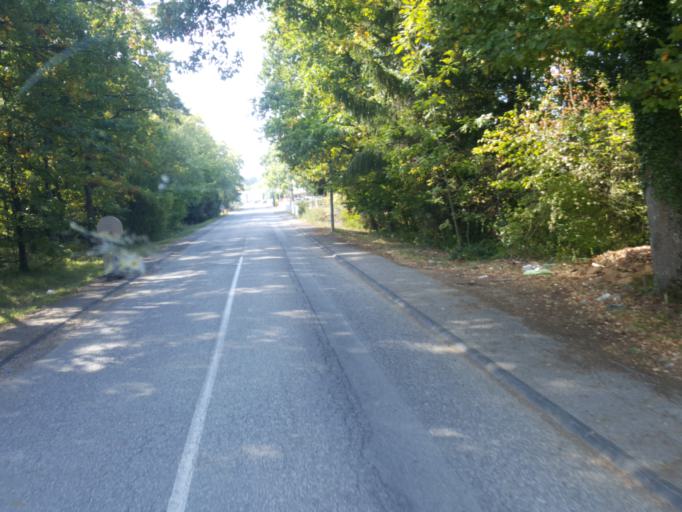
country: FR
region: Rhone-Alpes
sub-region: Departement de la Haute-Savoie
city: Ballaison
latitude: 46.2769
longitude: 6.3494
